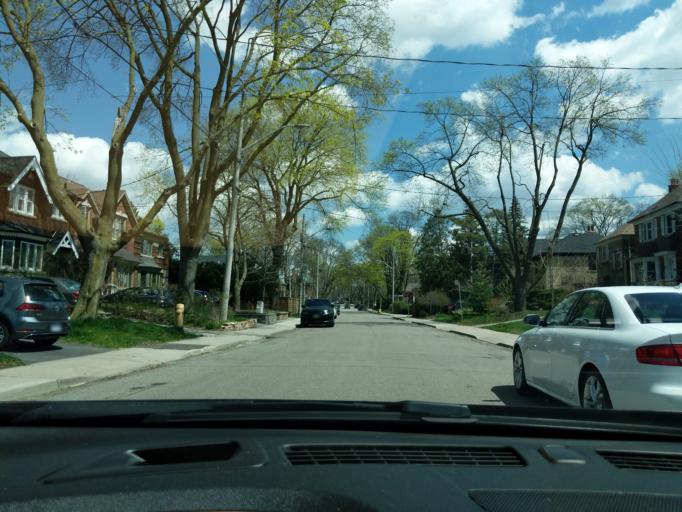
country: CA
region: Ontario
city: Toronto
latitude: 43.6990
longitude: -79.3711
